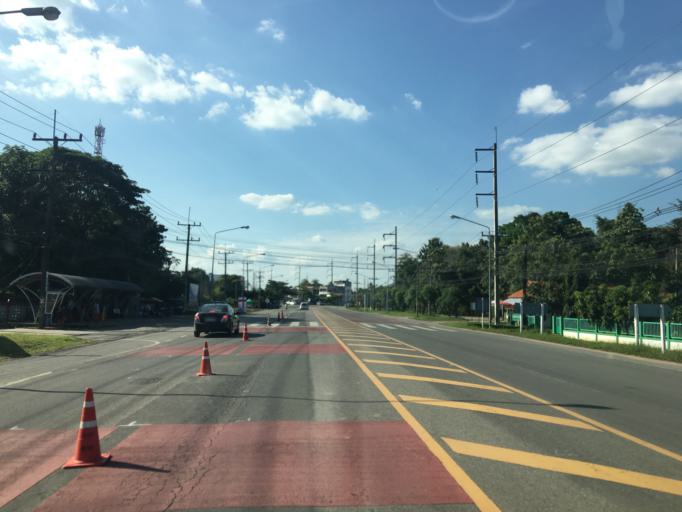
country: TH
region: Phayao
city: Chun
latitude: 19.3377
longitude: 100.1316
